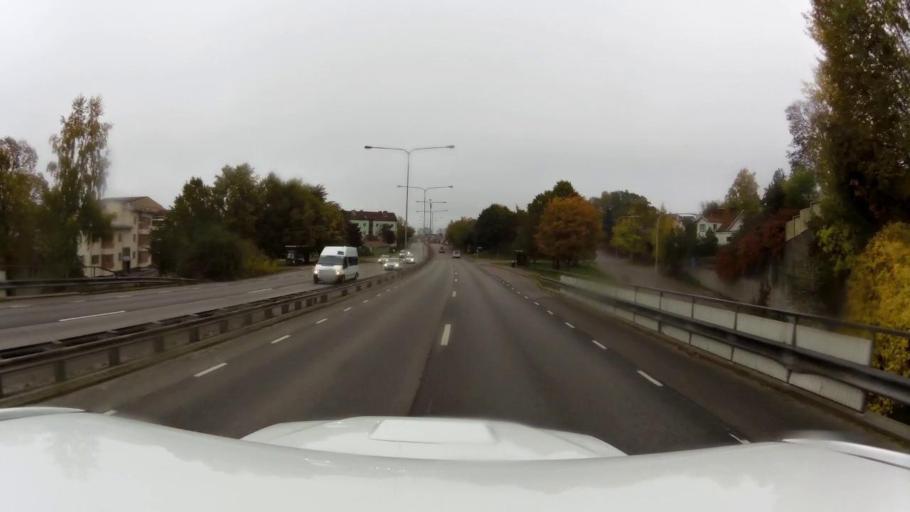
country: SE
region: OEstergoetland
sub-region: Linkopings Kommun
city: Linkoping
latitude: 58.3995
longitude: 15.6457
